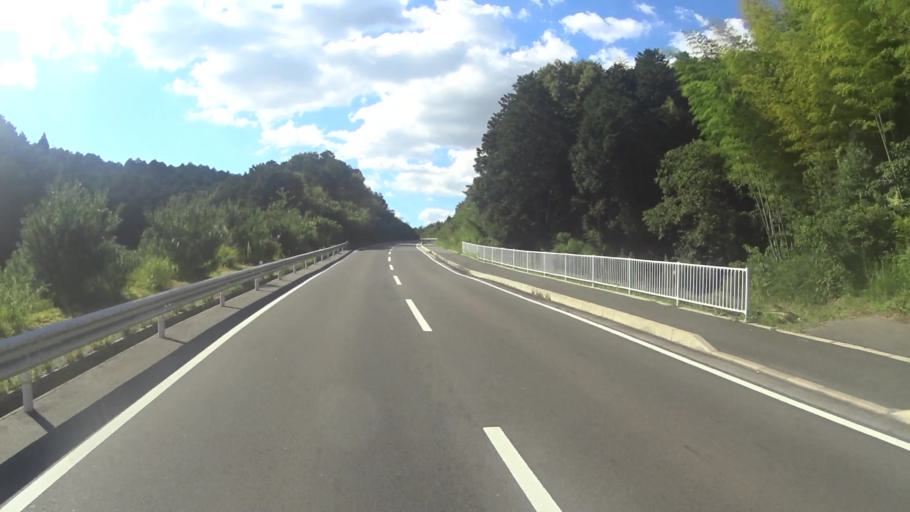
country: JP
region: Kyoto
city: Uji
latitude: 34.8399
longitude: 135.8509
